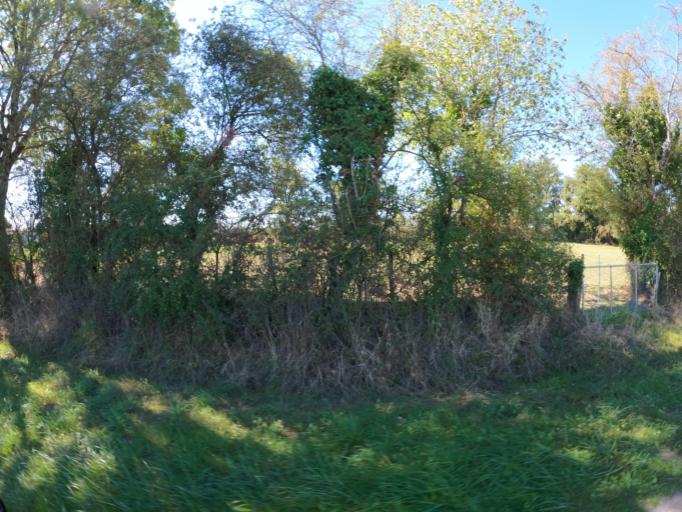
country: FR
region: Poitou-Charentes
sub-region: Departement de la Vienne
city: Lathus-Saint-Remy
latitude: 46.3018
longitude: 0.9912
